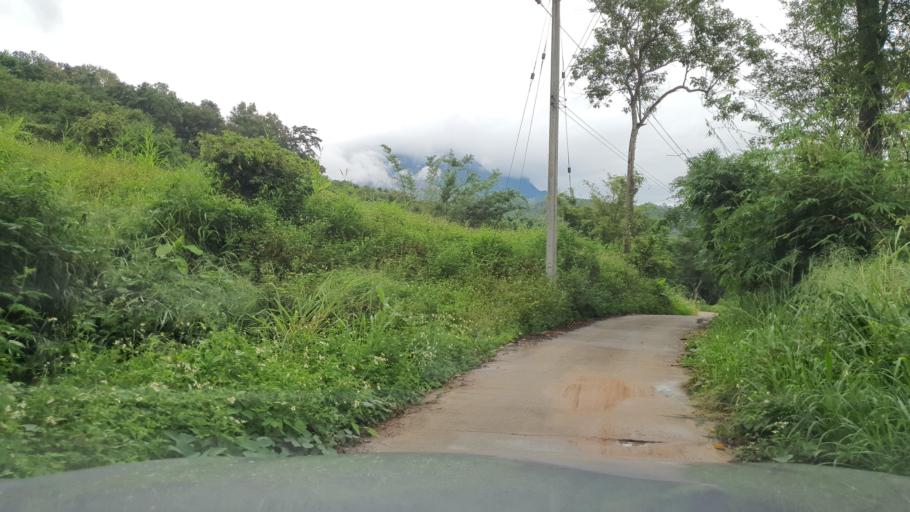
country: TH
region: Chiang Mai
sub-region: Amphoe Chiang Dao
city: Chiang Dao
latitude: 19.3316
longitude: 98.9289
